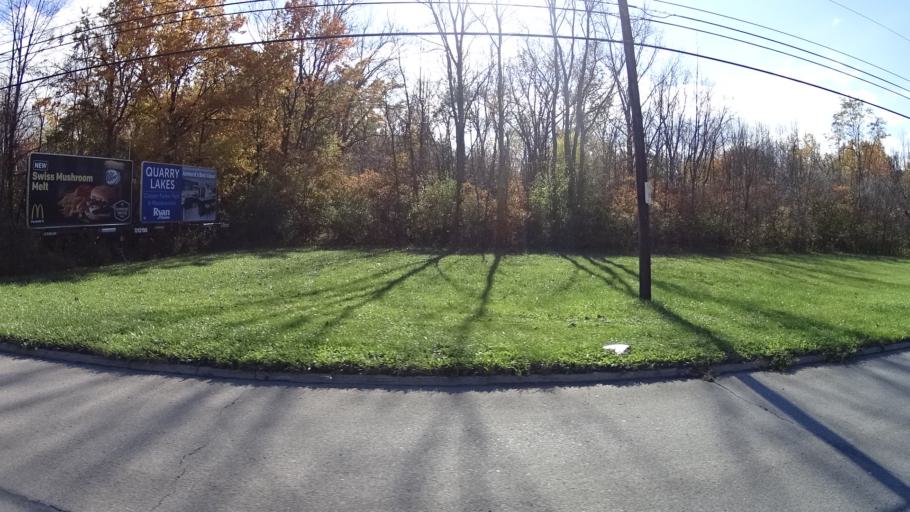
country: US
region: Ohio
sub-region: Lorain County
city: Lorain
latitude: 41.4508
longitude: -82.2069
